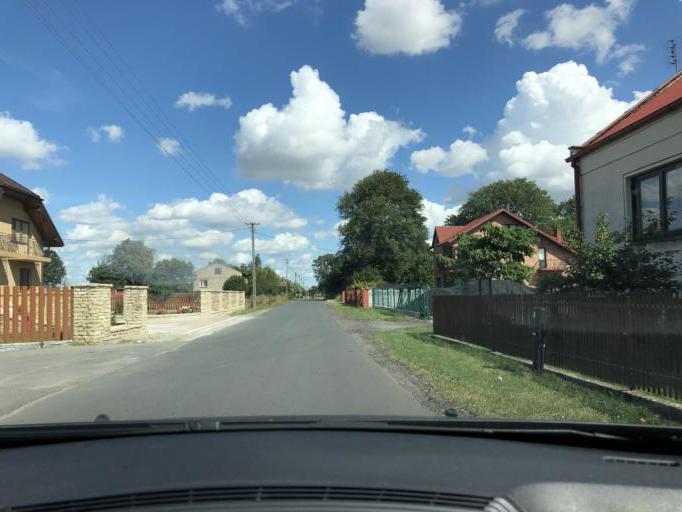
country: PL
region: Lodz Voivodeship
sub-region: Powiat wieruszowski
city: Czastary
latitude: 51.2330
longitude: 18.3555
